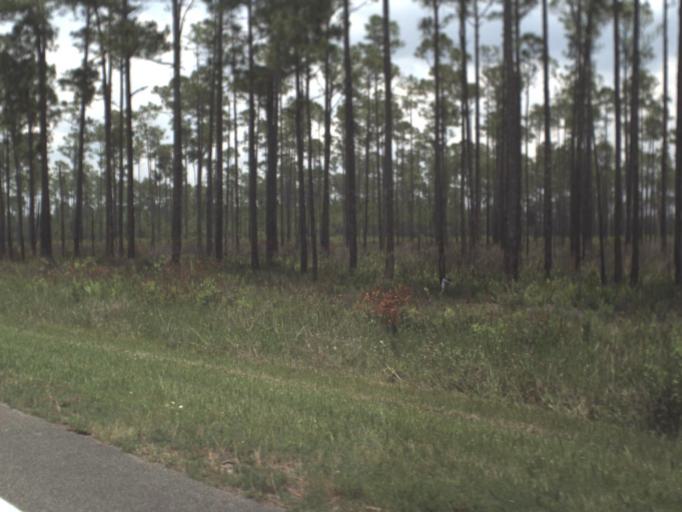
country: US
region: Florida
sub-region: Putnam County
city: Palatka
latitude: 29.4533
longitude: -81.7381
